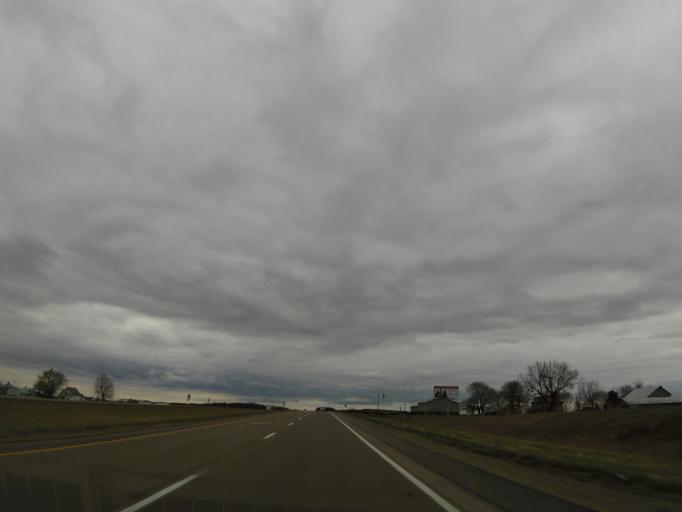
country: US
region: Iowa
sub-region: Henry County
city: Winfield
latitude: 41.2162
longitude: -91.5293
